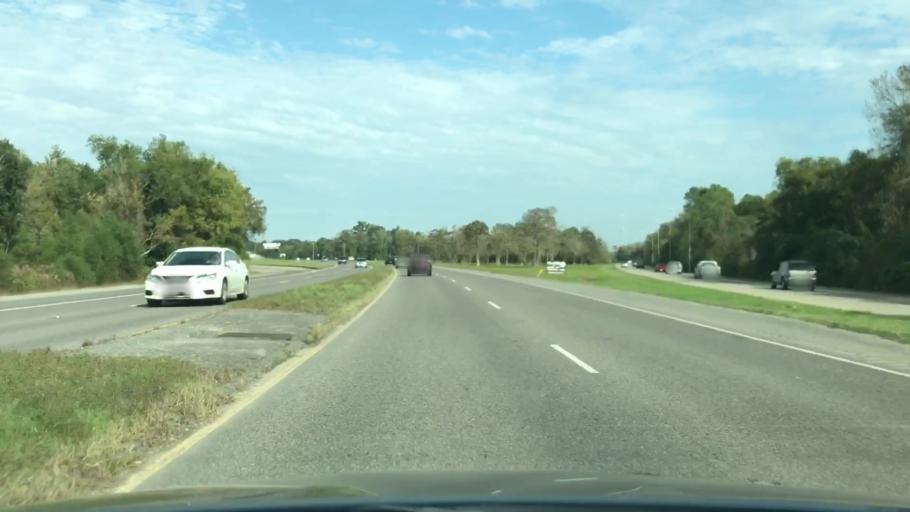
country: US
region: Louisiana
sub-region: Jefferson Parish
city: Avondale
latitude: 29.9106
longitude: -90.1808
